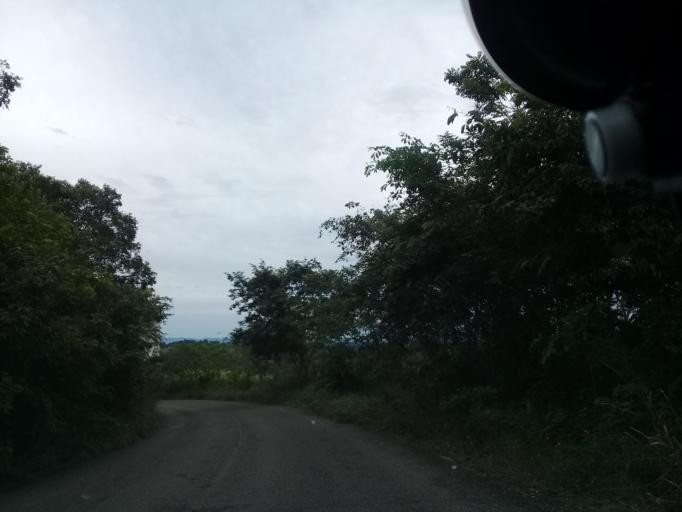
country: MX
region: Hidalgo
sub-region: Huejutla de Reyes
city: Chalahuiyapa
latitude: 21.2001
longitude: -98.3429
